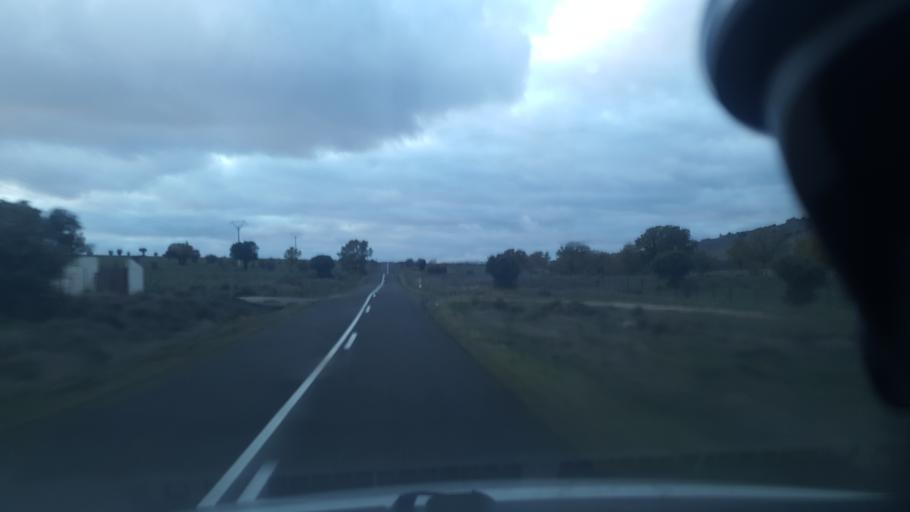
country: ES
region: Castille and Leon
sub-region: Provincia de Segovia
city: Ituero y Lama
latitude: 40.7051
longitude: -4.3436
